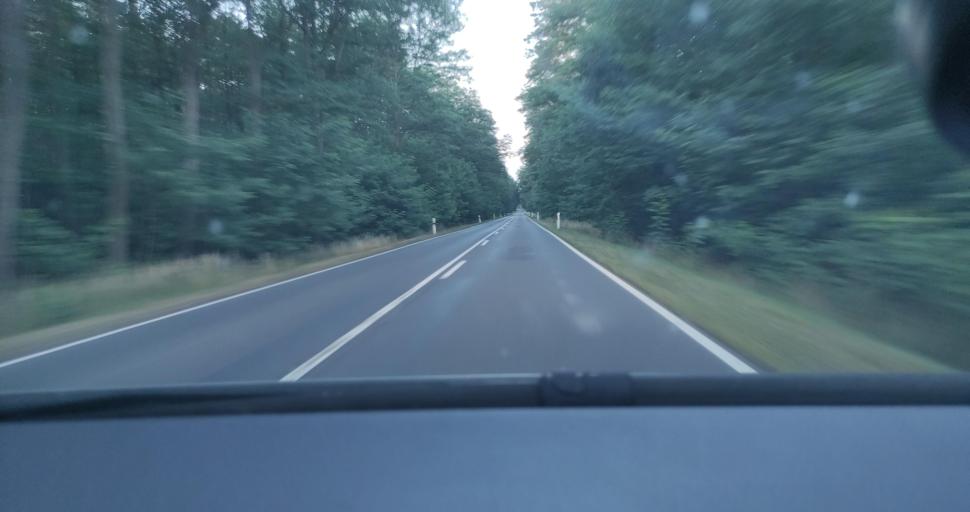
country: DE
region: Brandenburg
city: Forst
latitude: 51.7240
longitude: 14.5510
